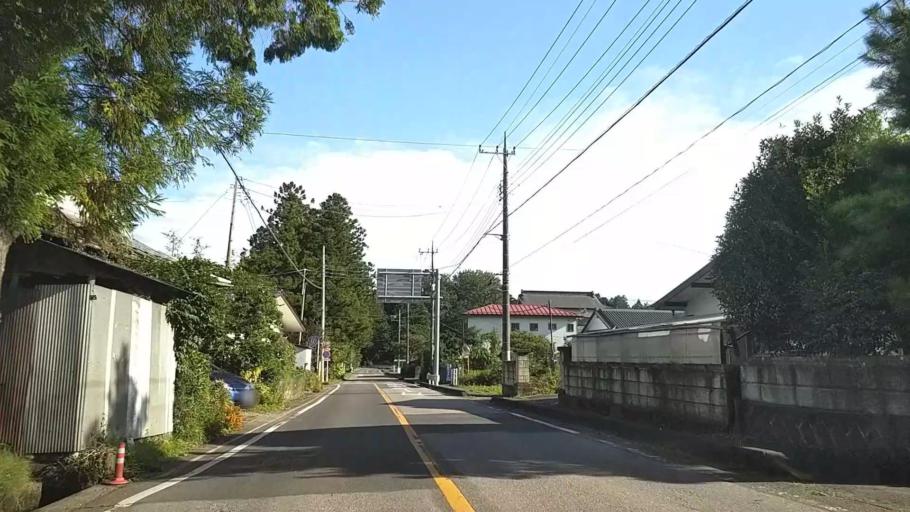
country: JP
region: Tochigi
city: Imaichi
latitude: 36.7611
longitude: 139.7083
